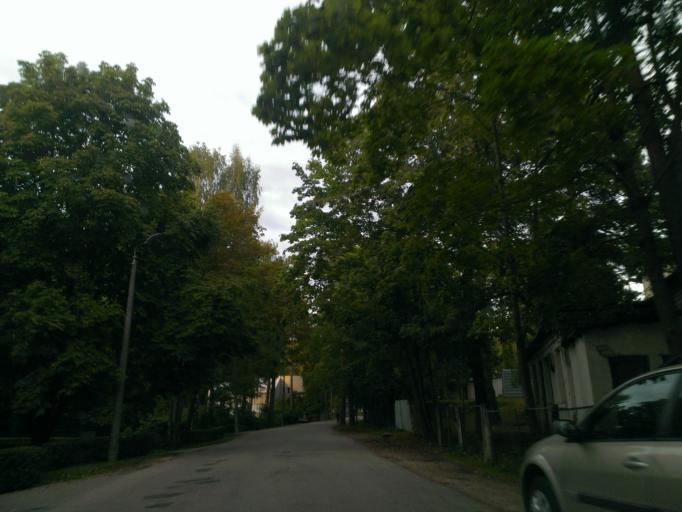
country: LV
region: Ogre
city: Ogre
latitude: 56.8192
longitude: 24.5974
